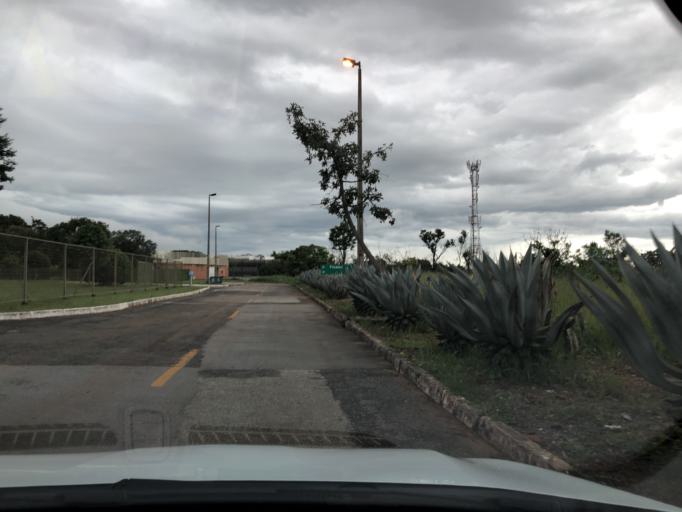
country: BR
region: Federal District
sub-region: Brasilia
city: Brasilia
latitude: -15.7737
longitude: -47.8702
